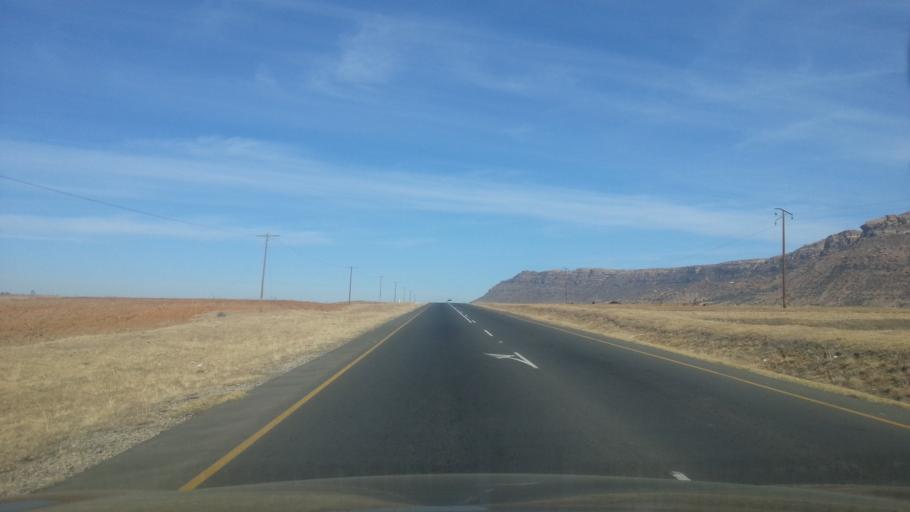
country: LS
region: Maseru
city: Maseru
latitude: -29.4714
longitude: 27.5330
